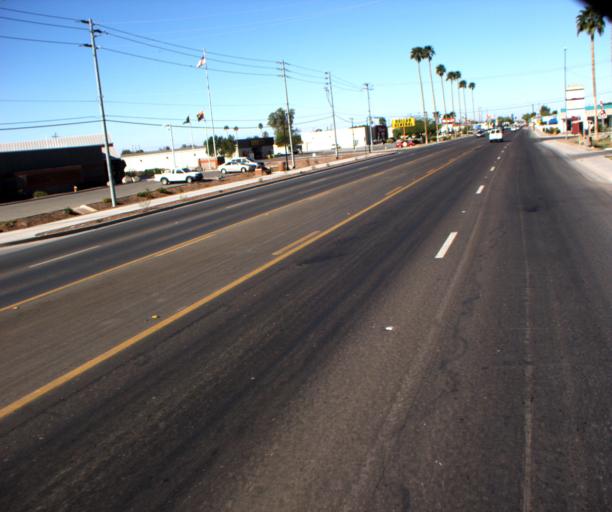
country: US
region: Arizona
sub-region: Yuma County
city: Somerton
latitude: 32.5967
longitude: -114.7053
